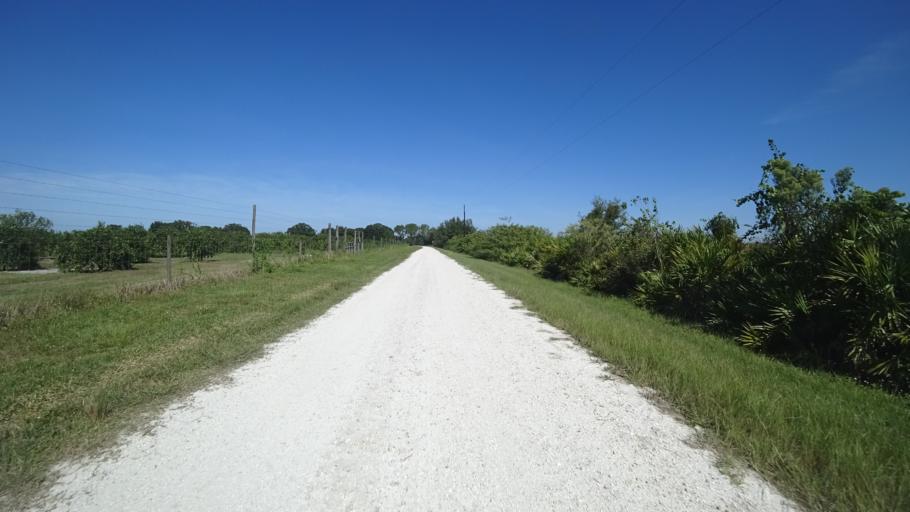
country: US
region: Florida
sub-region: Hillsborough County
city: Wimauma
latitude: 27.5353
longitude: -82.0877
